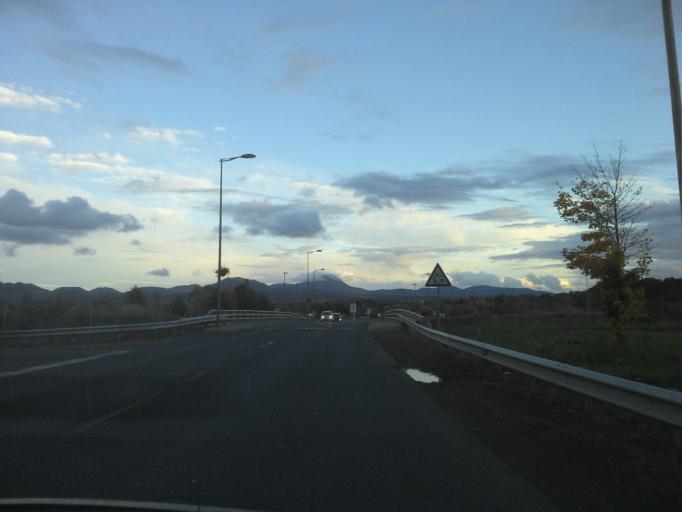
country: FR
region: Auvergne
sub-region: Departement du Puy-de-Dome
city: Chapdes-Beaufort
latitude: 45.8371
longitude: 2.8232
